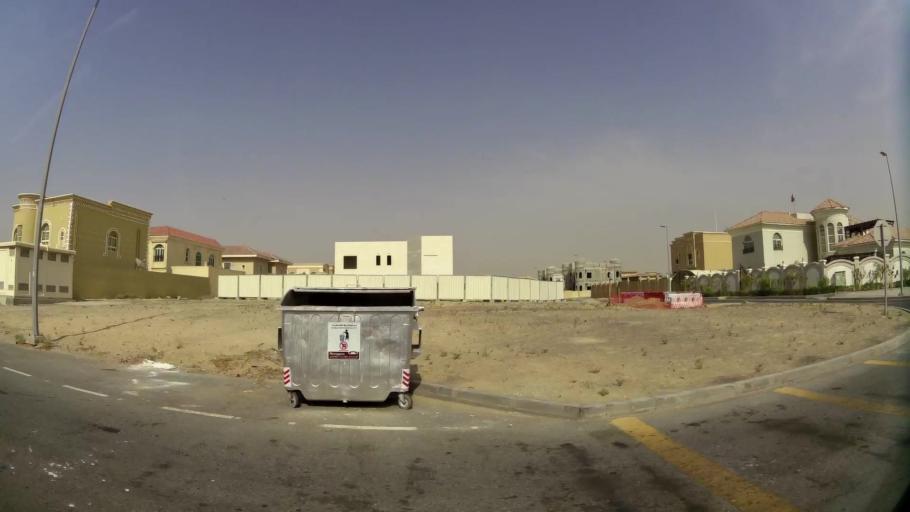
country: AE
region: Ash Shariqah
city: Sharjah
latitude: 25.2626
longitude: 55.4595
